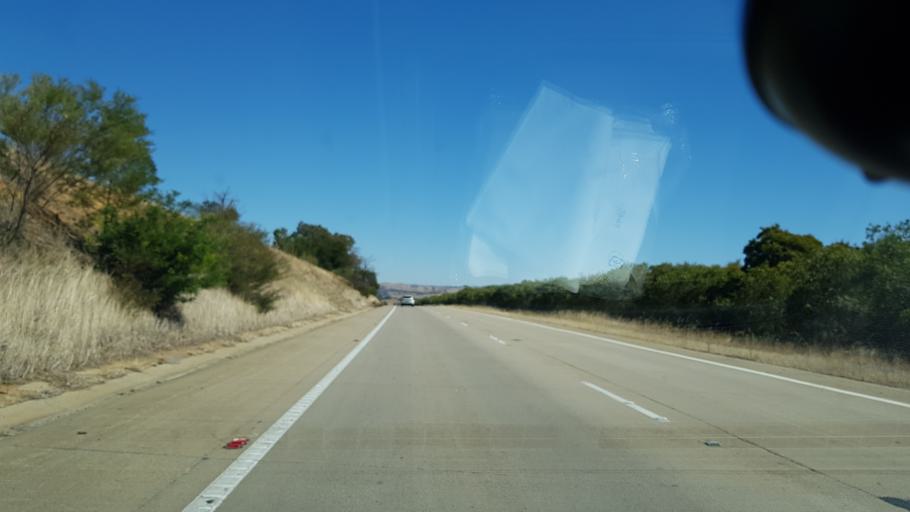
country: AU
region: New South Wales
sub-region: Gundagai
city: Gundagai
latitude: -34.8162
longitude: 148.3989
